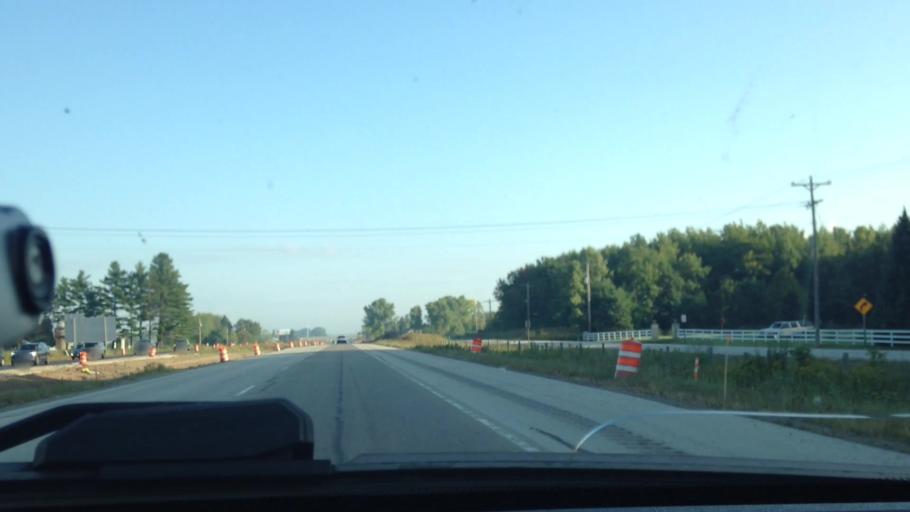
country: US
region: Wisconsin
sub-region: Brown County
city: Suamico
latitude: 44.6517
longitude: -88.0492
